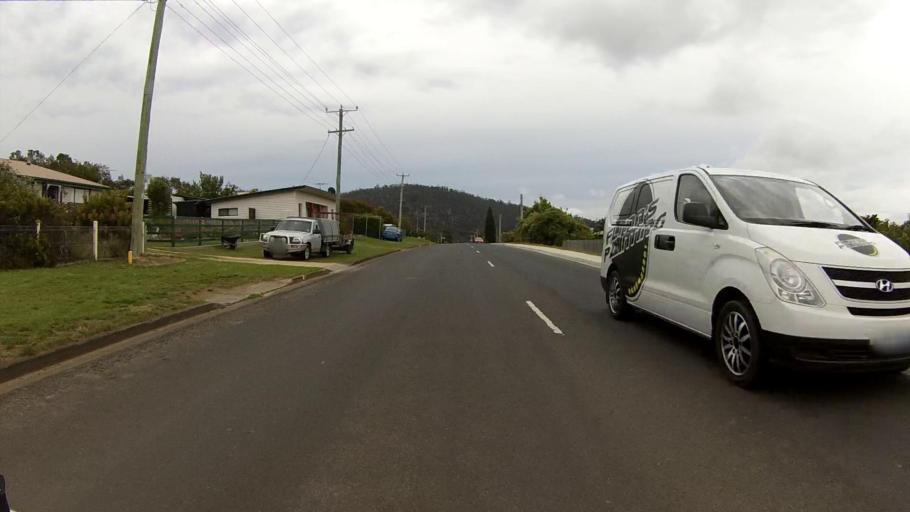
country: AU
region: Tasmania
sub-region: Sorell
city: Sorell
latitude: -42.5658
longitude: 147.8737
